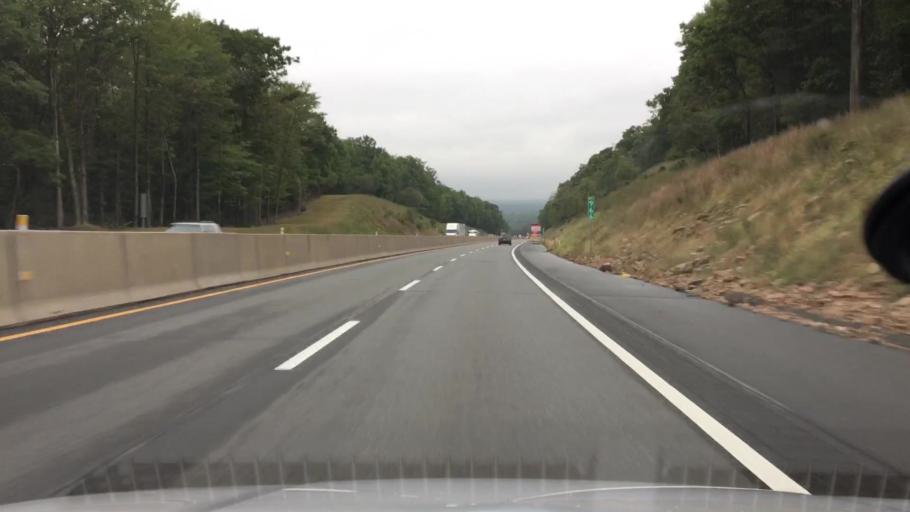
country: US
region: Pennsylvania
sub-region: Luzerne County
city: White Haven
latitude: 41.0852
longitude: -75.7370
